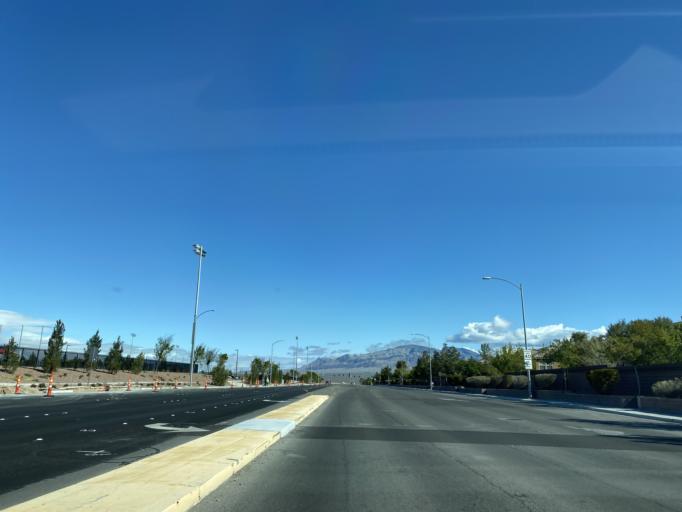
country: US
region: Nevada
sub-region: Clark County
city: Summerlin South
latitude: 36.3178
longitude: -115.2967
